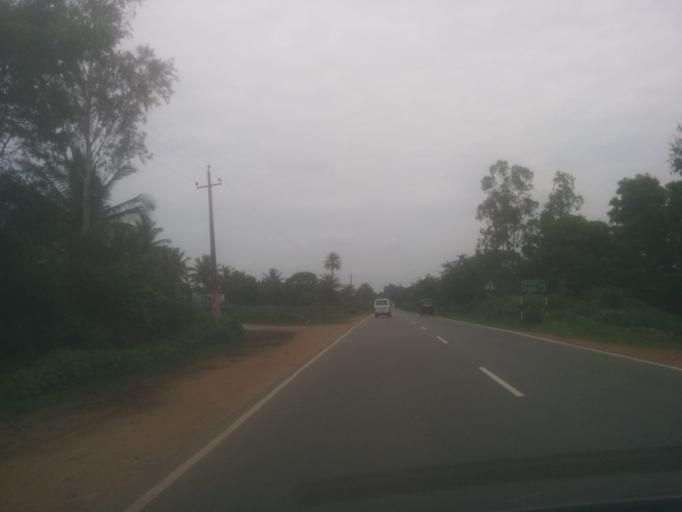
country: IN
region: Karnataka
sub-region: Hassan
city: Belur
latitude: 13.1632
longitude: 75.8844
